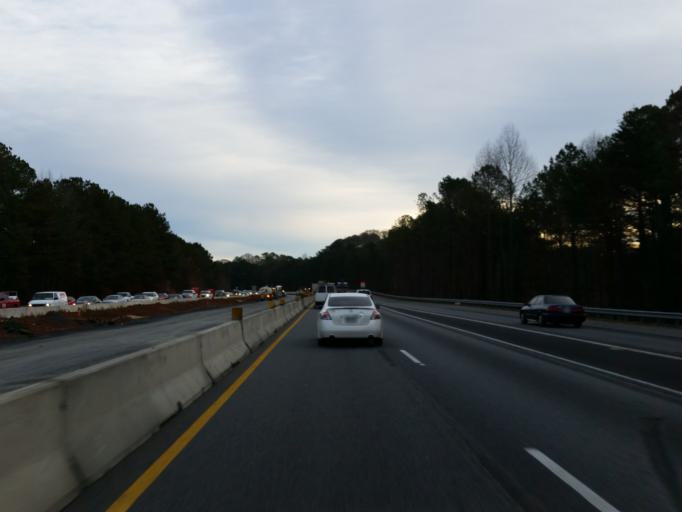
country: US
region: Georgia
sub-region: Cherokee County
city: Woodstock
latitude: 34.0534
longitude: -84.5509
